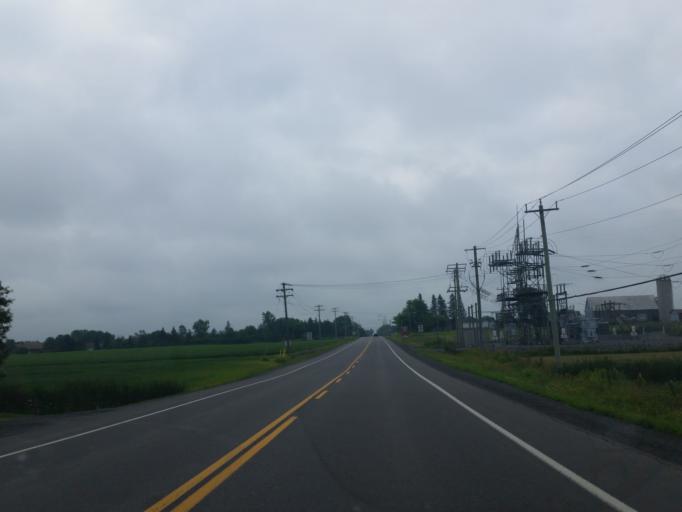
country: CA
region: Ontario
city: Clarence-Rockland
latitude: 45.4300
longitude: -75.4317
